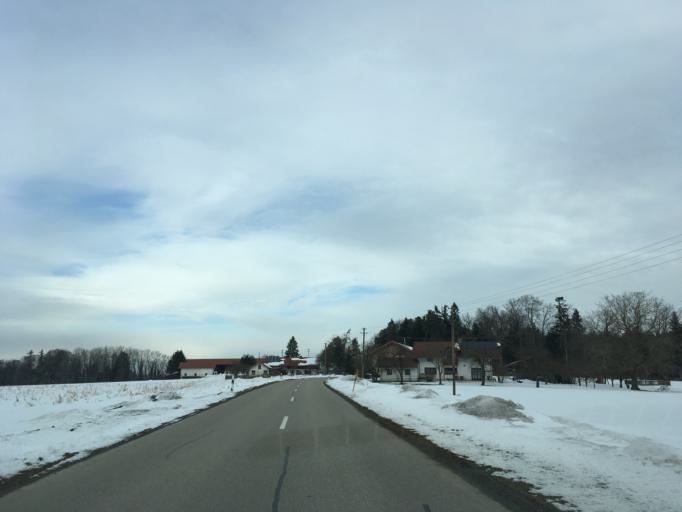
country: DE
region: Bavaria
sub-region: Upper Bavaria
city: Schnaitsee
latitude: 48.0935
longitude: 12.3621
